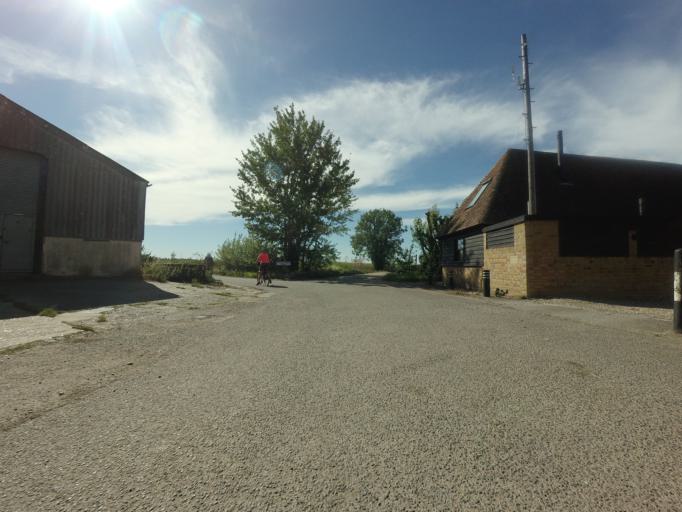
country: GB
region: England
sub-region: Kent
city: Birchington-on-Sea
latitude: 51.3629
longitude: 1.2375
